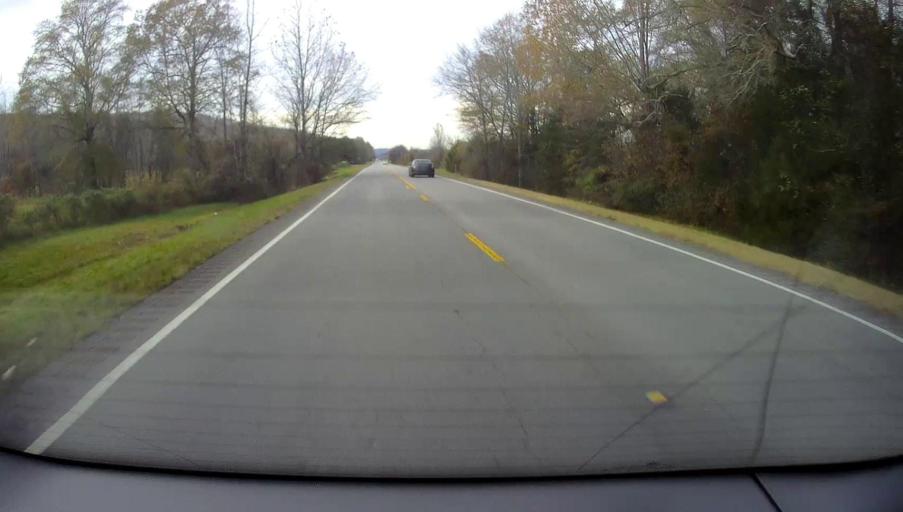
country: US
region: Alabama
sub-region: Marshall County
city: Arab
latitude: 34.3942
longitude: -86.6747
